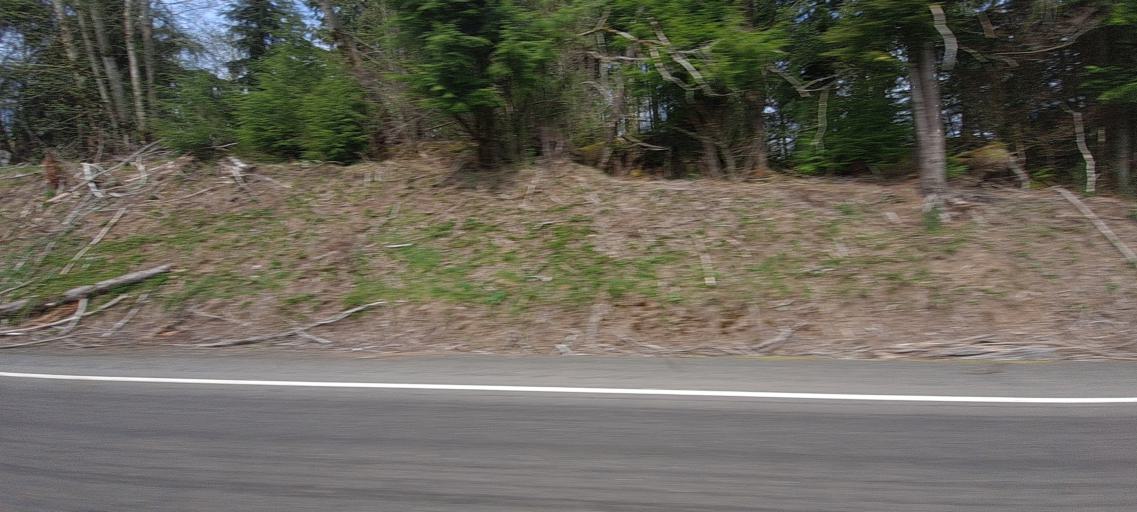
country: US
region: Oregon
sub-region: Clatsop County
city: Seaside
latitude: 45.9025
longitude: -123.6630
